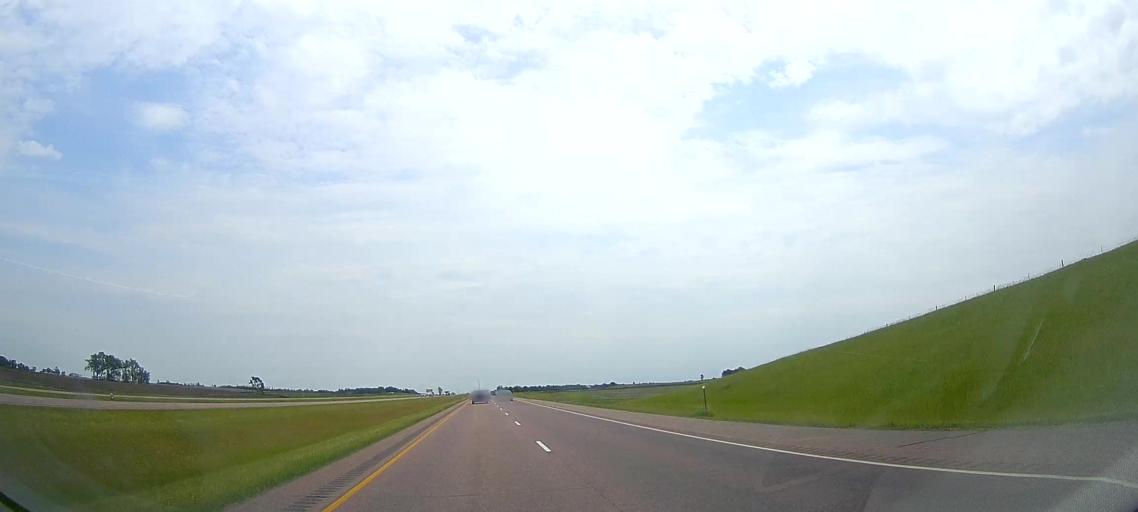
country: US
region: South Dakota
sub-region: Minnehaha County
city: Hartford
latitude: 43.6559
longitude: -97.1055
